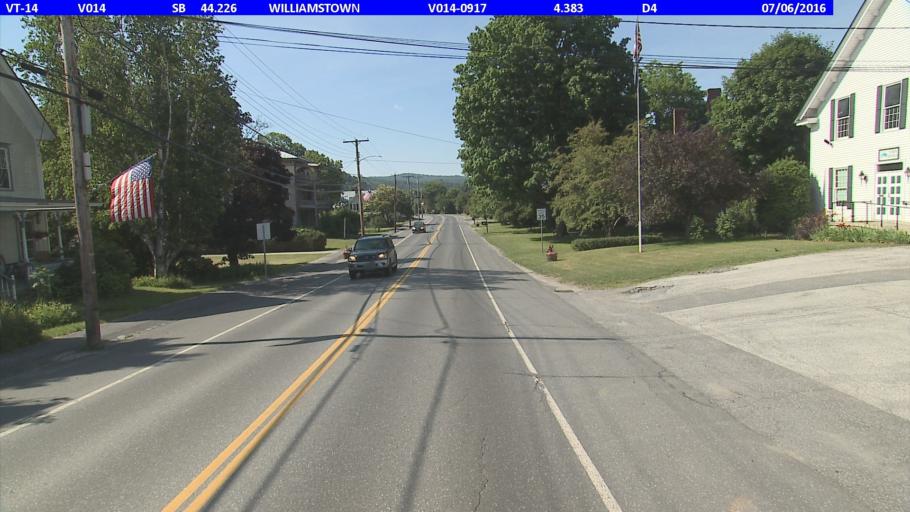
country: US
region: Vermont
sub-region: Orange County
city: Williamstown
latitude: 44.1208
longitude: -72.5412
